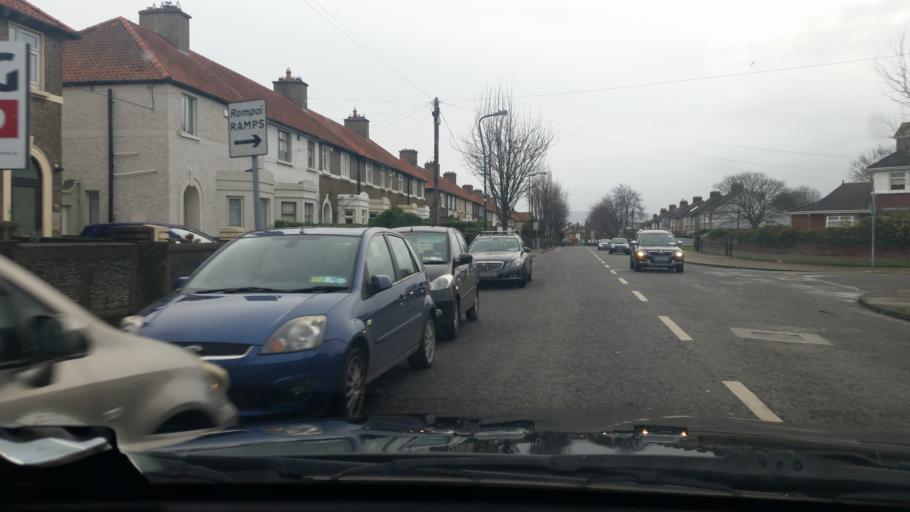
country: IE
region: Leinster
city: Marino
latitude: 53.3700
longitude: -6.2389
